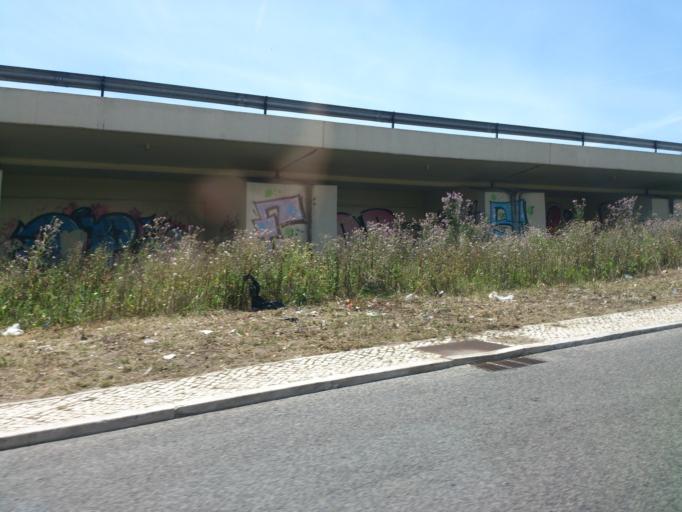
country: PT
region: Lisbon
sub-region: Oeiras
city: Quejas
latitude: 38.7003
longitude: -9.2608
